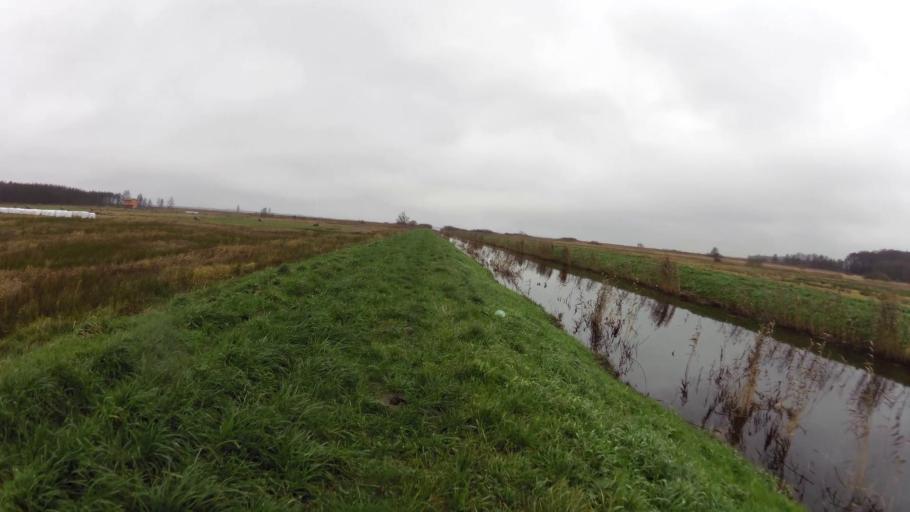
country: PL
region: West Pomeranian Voivodeship
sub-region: Koszalin
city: Koszalin
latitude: 54.2474
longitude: 16.1311
